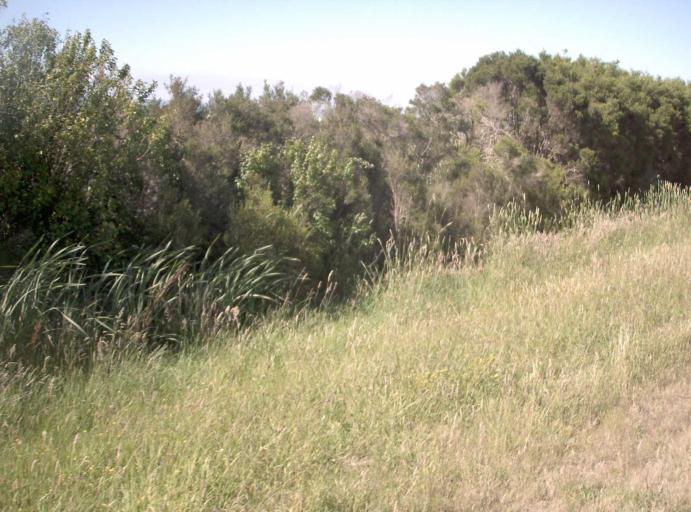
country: AU
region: Victoria
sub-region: Latrobe
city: Traralgon
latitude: -38.6302
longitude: 146.5951
